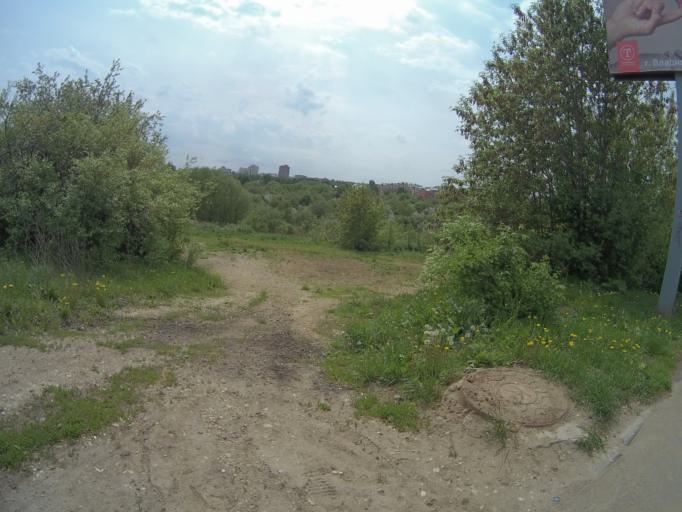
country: RU
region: Vladimir
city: Vladimir
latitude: 56.1360
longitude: 40.3880
